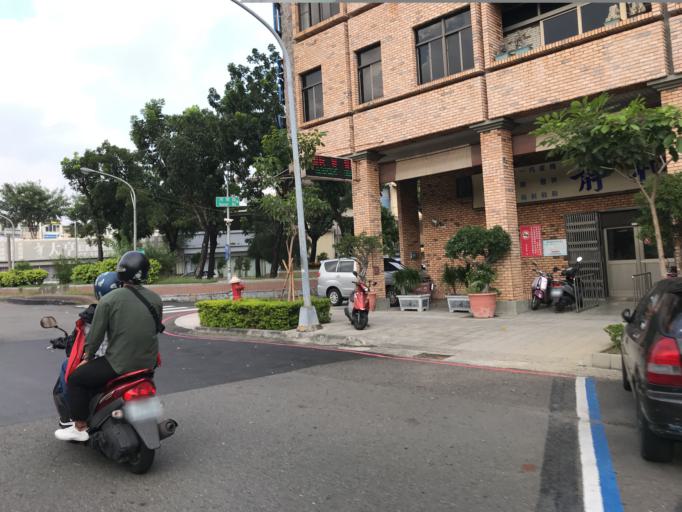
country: TW
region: Kaohsiung
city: Kaohsiung
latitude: 22.6360
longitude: 120.3139
